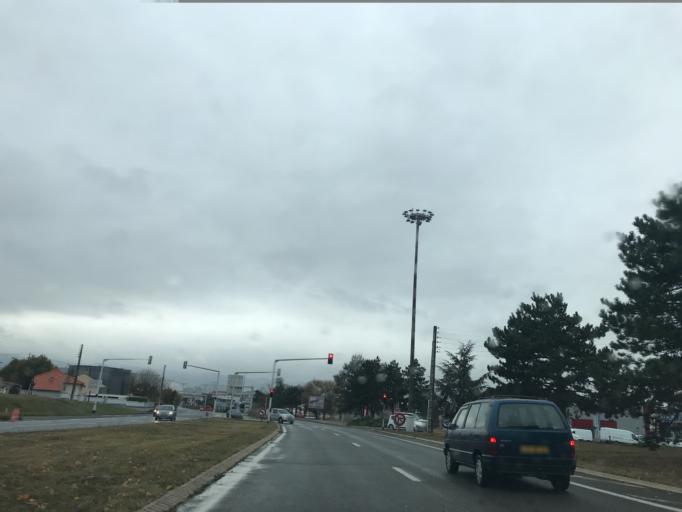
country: FR
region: Auvergne
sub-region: Departement du Puy-de-Dome
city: Aubiere
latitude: 45.7786
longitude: 3.1271
